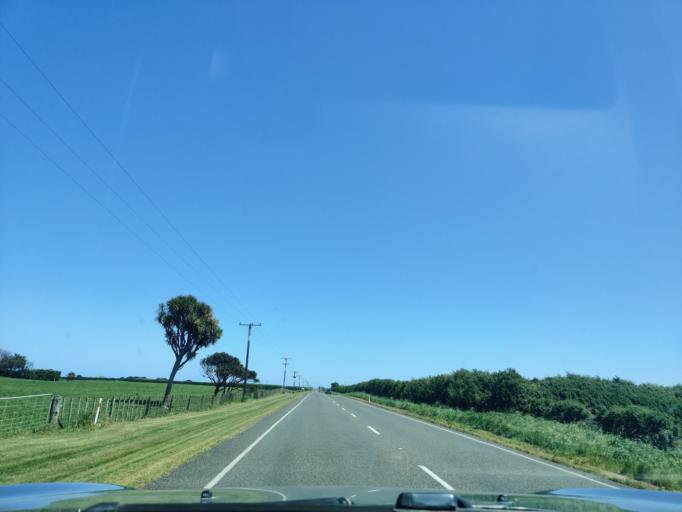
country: NZ
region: Taranaki
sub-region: South Taranaki District
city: Patea
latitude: -39.7466
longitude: 174.5135
